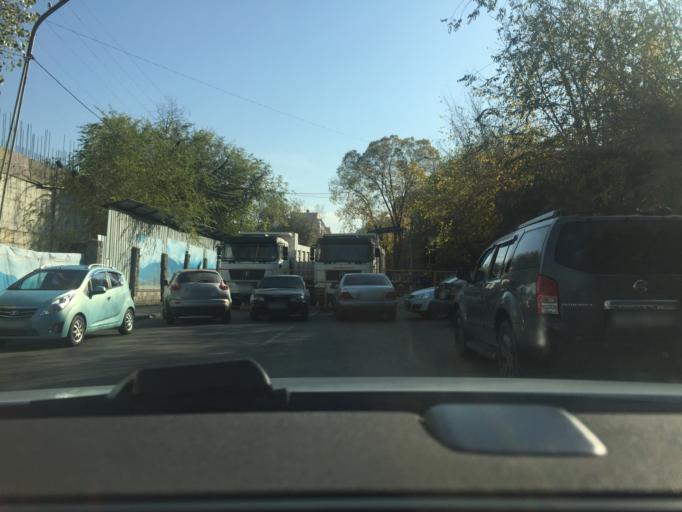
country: KZ
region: Almaty Qalasy
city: Almaty
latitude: 43.2468
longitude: 76.9294
